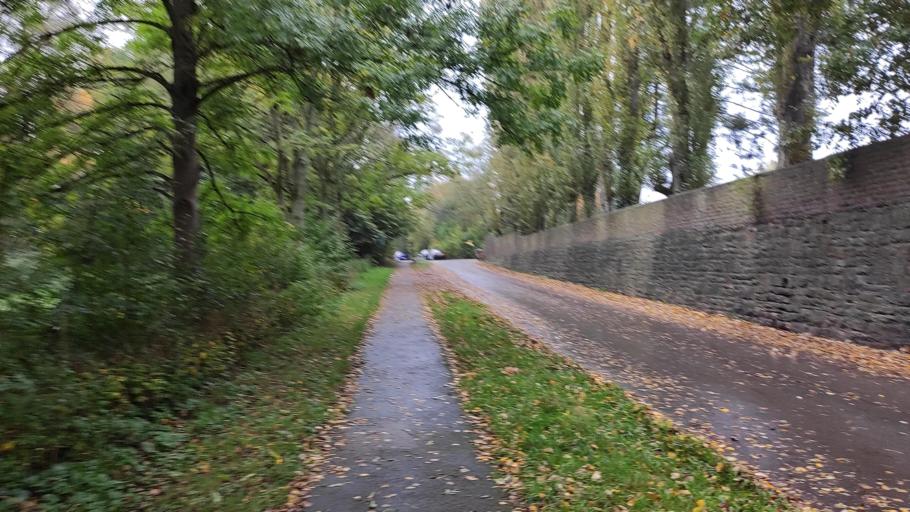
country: DE
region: North Rhine-Westphalia
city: Sprockhovel
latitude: 51.4219
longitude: 7.2738
